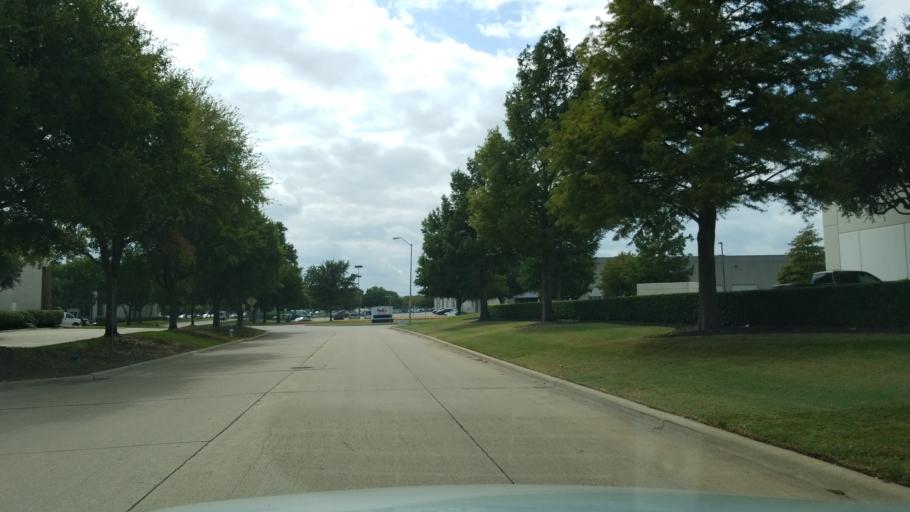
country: US
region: Texas
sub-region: Dallas County
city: Garland
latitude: 32.8941
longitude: -96.6787
